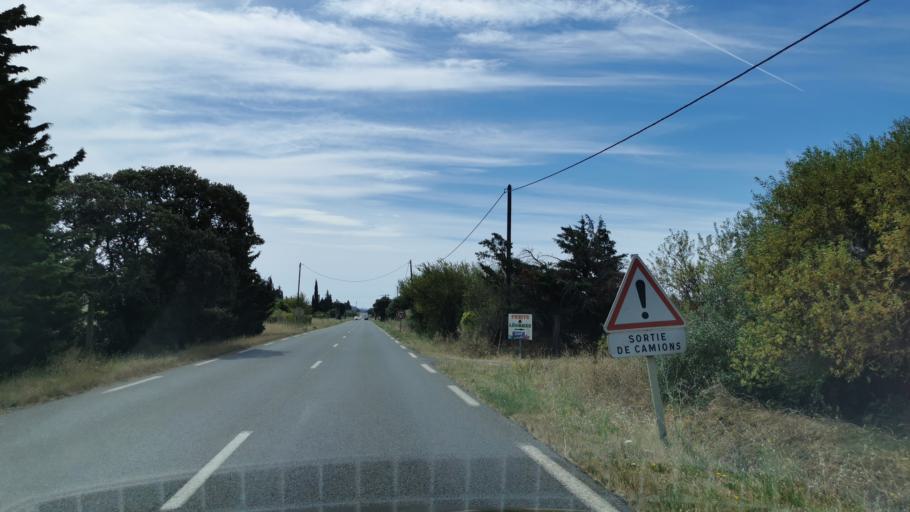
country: FR
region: Languedoc-Roussillon
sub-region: Departement de l'Aude
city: Ginestas
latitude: 43.2674
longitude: 2.8977
